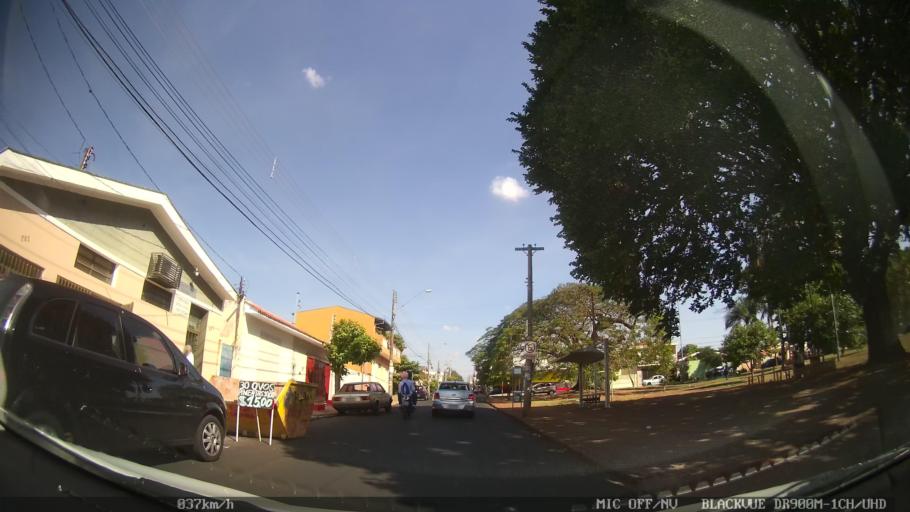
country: BR
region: Sao Paulo
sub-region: Ribeirao Preto
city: Ribeirao Preto
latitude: -21.1826
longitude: -47.8250
